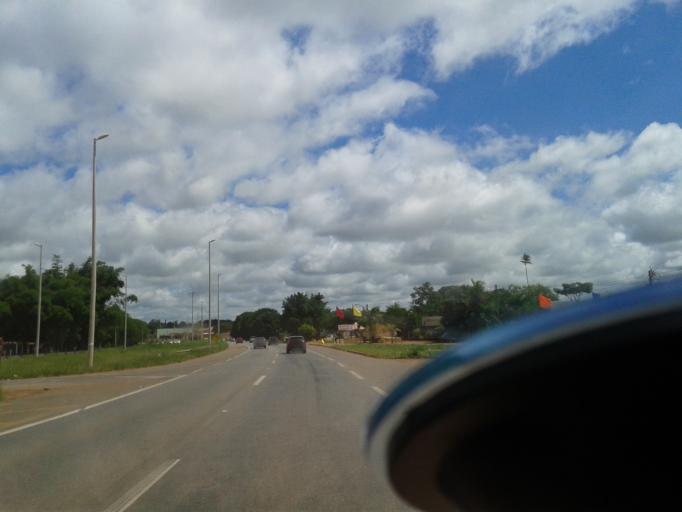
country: BR
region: Goias
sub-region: Goianira
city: Goianira
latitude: -16.5466
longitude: -49.4041
